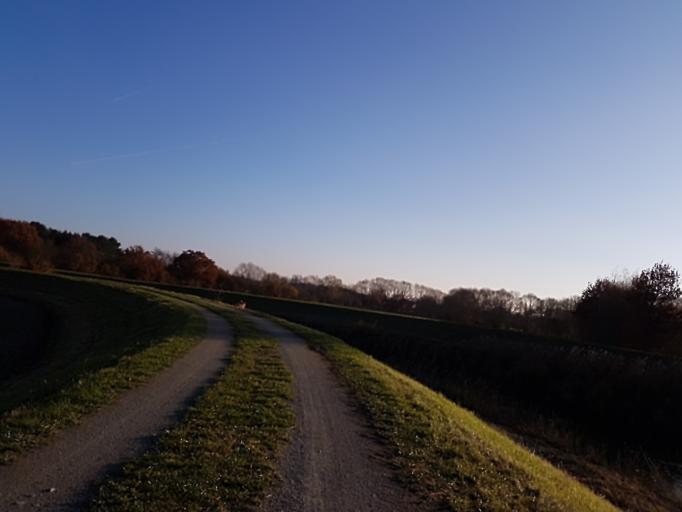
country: BE
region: Flanders
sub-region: Provincie Vlaams-Brabant
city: Boortmeerbeek
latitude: 50.9922
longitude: 4.6011
